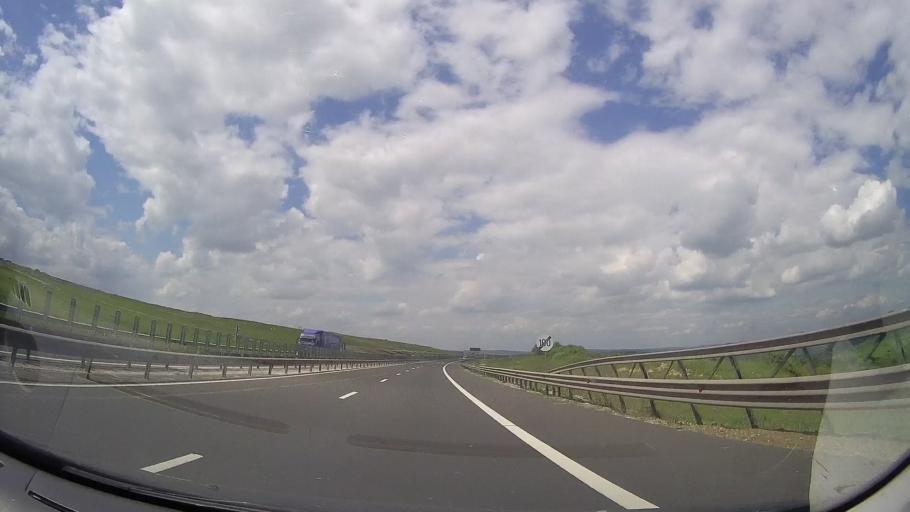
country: RO
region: Sibiu
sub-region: Comuna Tilisca
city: Tilisca
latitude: 45.8299
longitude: 23.8631
